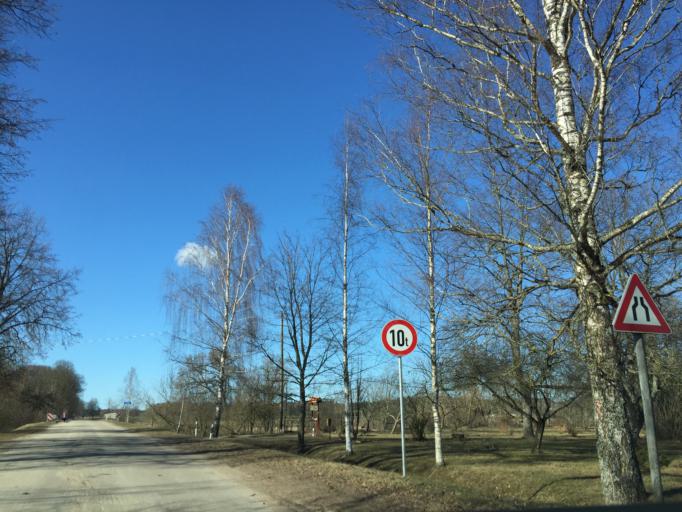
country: LV
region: Ogre
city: Ogre
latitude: 56.8571
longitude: 24.6990
